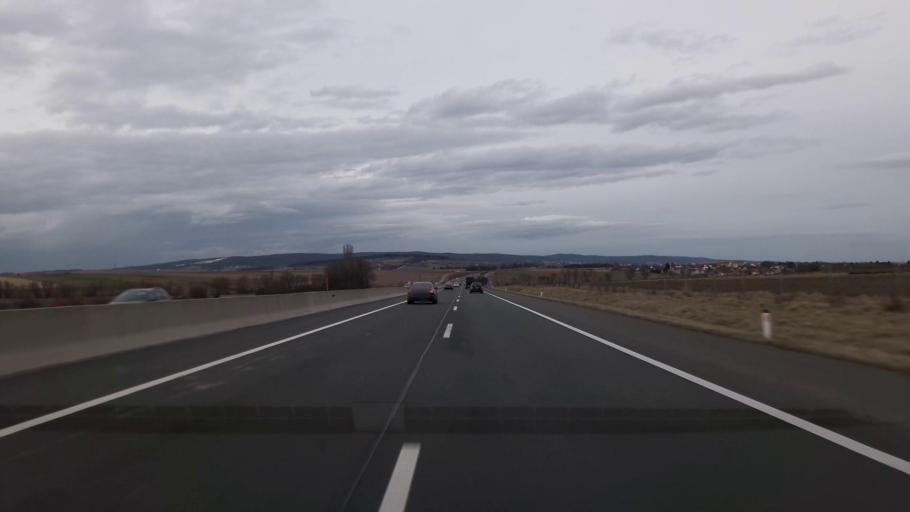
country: AT
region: Burgenland
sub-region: Politischer Bezirk Mattersburg
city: Hirm
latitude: 47.7818
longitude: 16.4374
